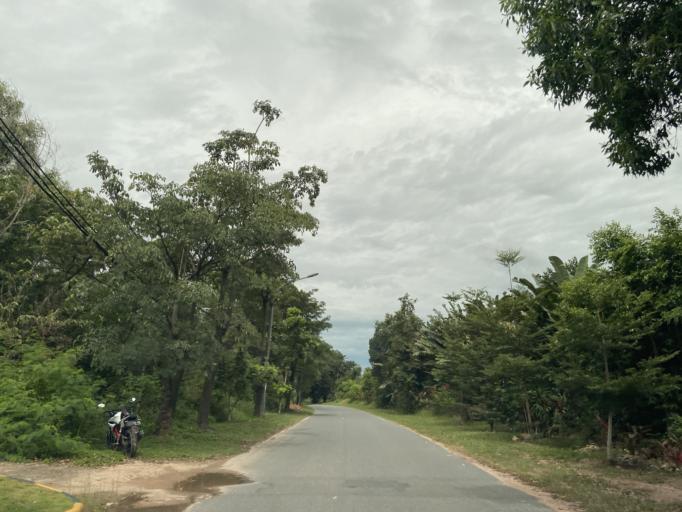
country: SG
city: Singapore
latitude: 1.1056
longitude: 104.0335
